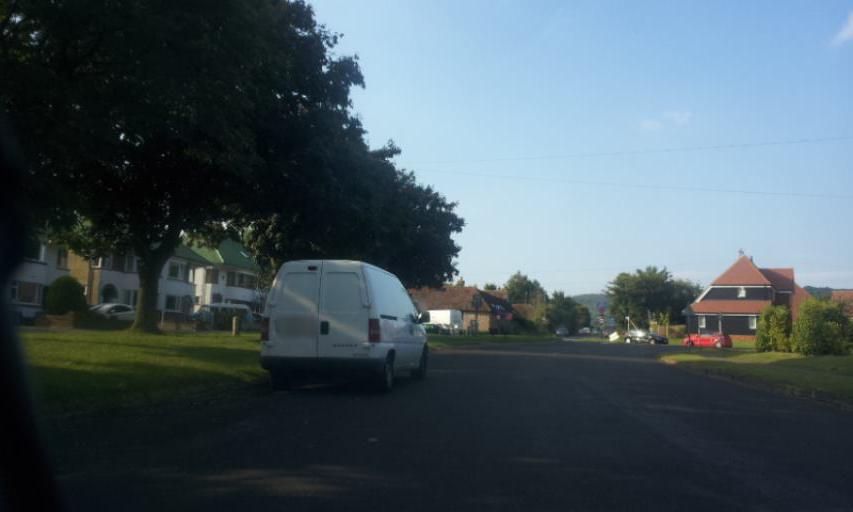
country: GB
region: England
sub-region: Kent
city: Boxley
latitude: 51.3046
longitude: 0.5142
